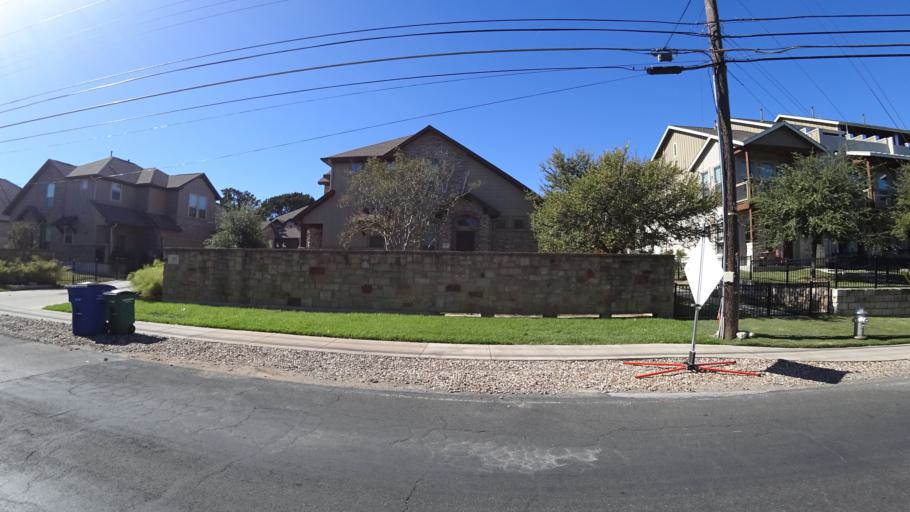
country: US
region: Texas
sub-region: Travis County
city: Rollingwood
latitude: 30.2441
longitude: -97.7768
